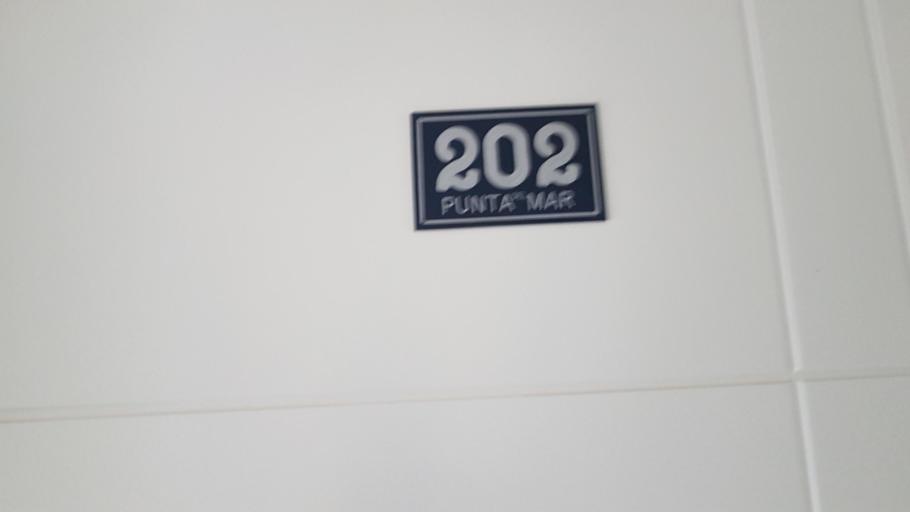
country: PE
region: Arequipa
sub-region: Provincia de Islay
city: Punta de Bombon
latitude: -17.1703
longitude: -71.7917
